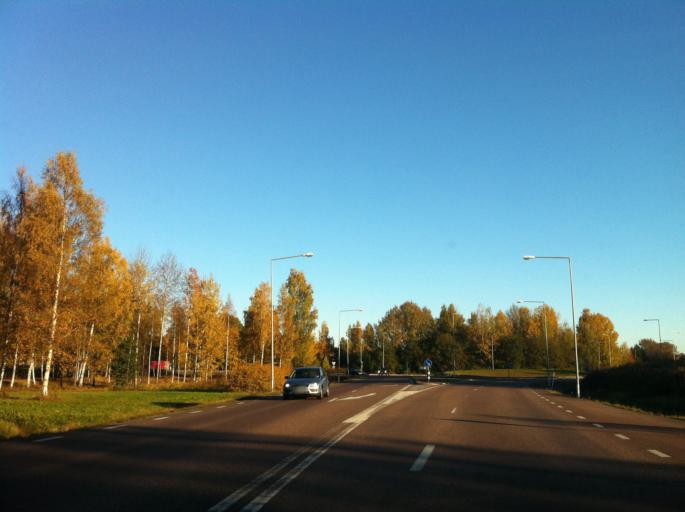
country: SE
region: Dalarna
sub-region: Faluns Kommun
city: Falun
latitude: 60.6265
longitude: 15.6093
